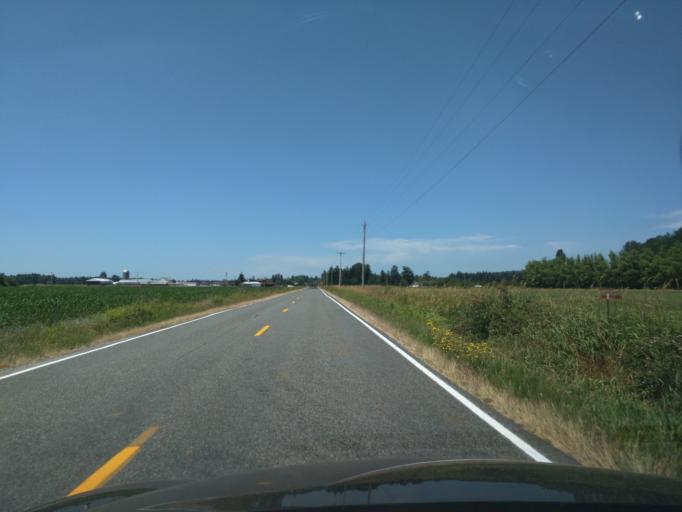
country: US
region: Washington
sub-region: Whatcom County
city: Ferndale
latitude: 48.9646
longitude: -122.5905
